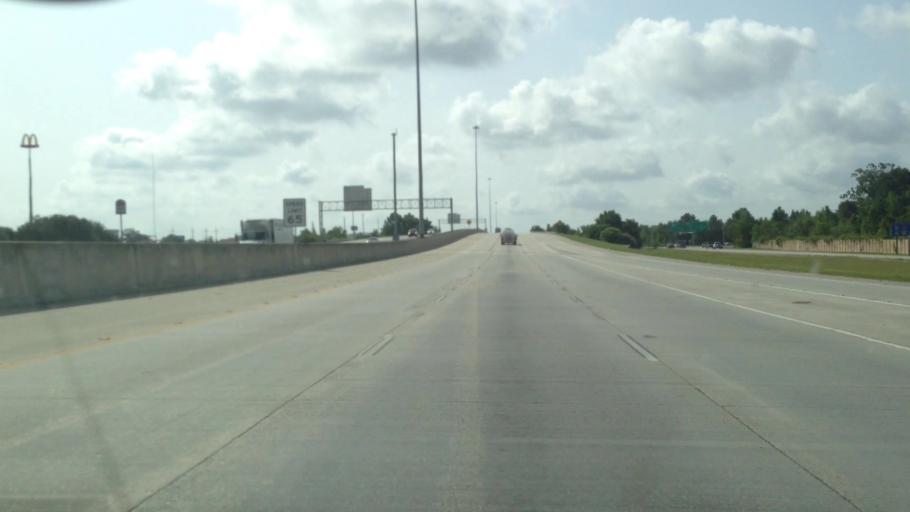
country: US
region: Louisiana
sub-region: East Baton Rouge Parish
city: Village Saint George
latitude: 30.3846
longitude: -91.0697
